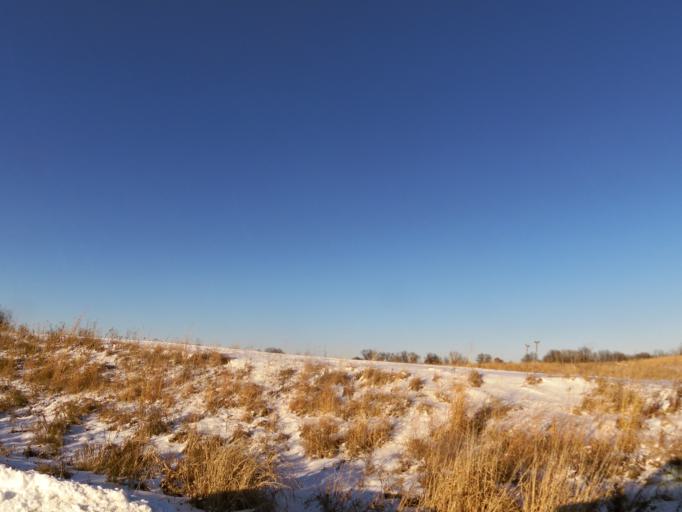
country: US
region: Minnesota
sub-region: Washington County
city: Lake Elmo
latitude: 44.9821
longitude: -92.9036
